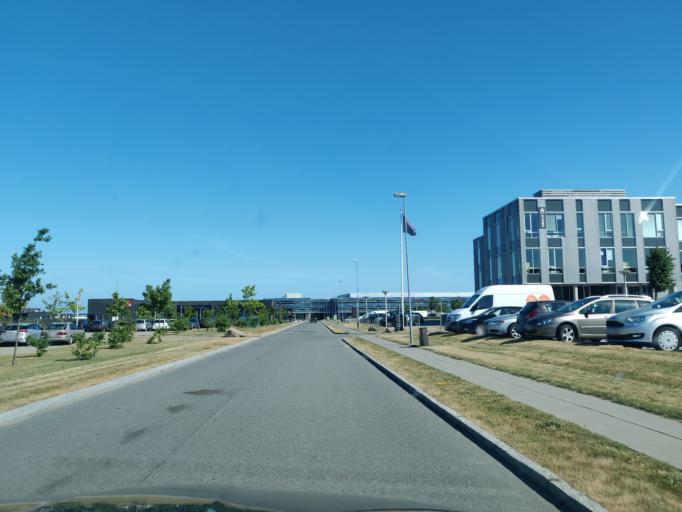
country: DK
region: Central Jutland
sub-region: Arhus Kommune
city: Arhus
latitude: 56.1931
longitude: 10.1835
